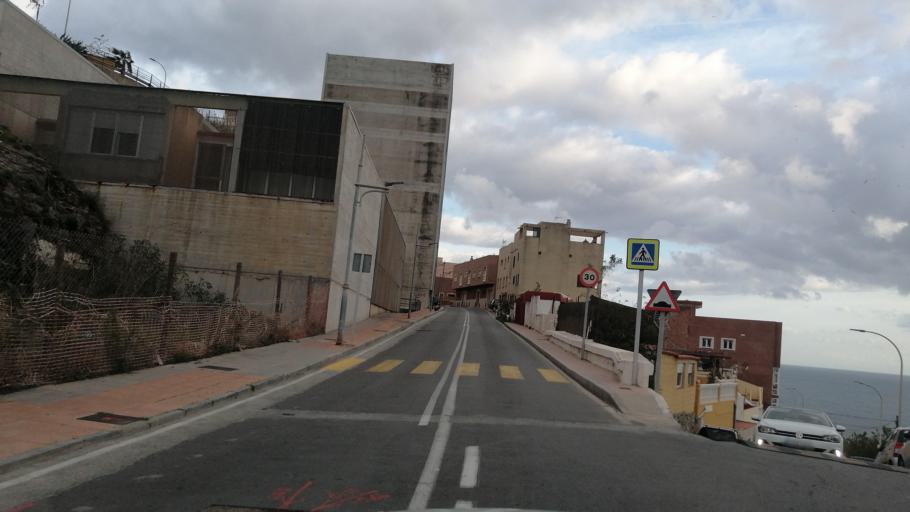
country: ES
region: Ceuta
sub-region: Ceuta
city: Ceuta
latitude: 35.8908
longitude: -5.2962
